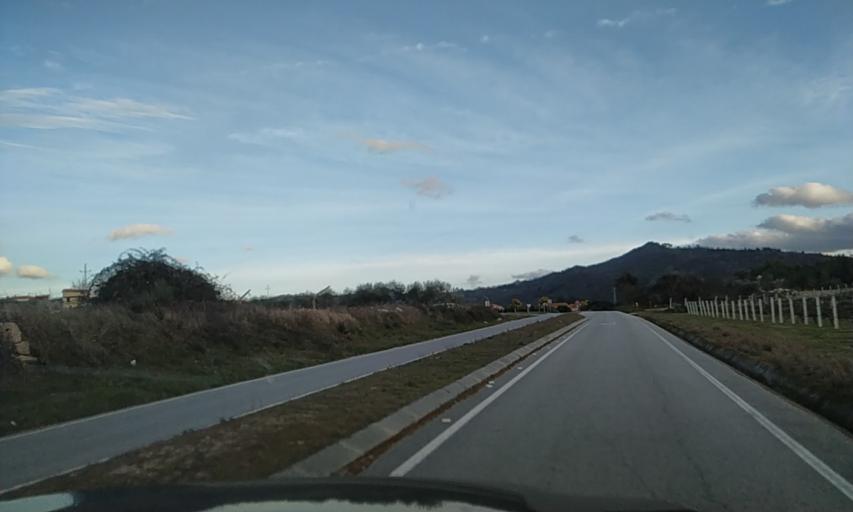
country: PT
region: Braganca
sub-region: Carrazeda de Ansiaes
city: Carrazeda de Anciaes
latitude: 41.2775
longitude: -7.3300
